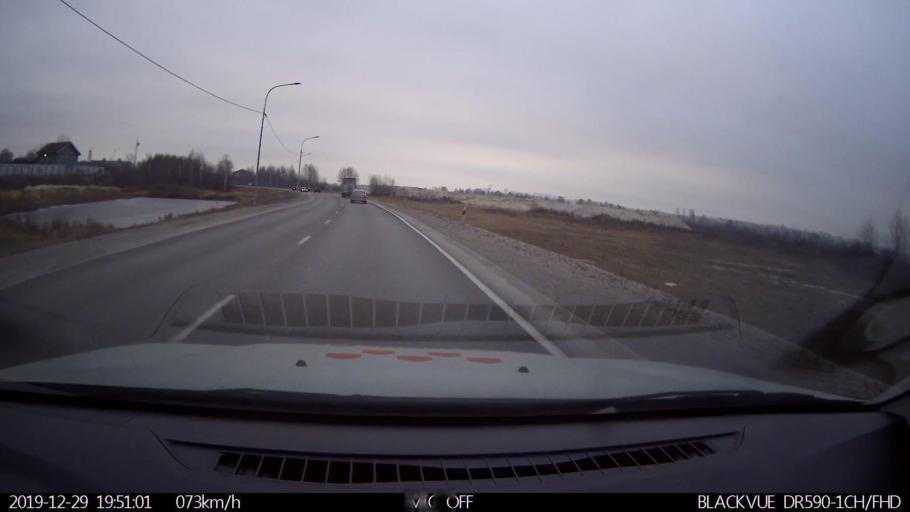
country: RU
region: Nizjnij Novgorod
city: Bor
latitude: 56.3623
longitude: 44.0339
